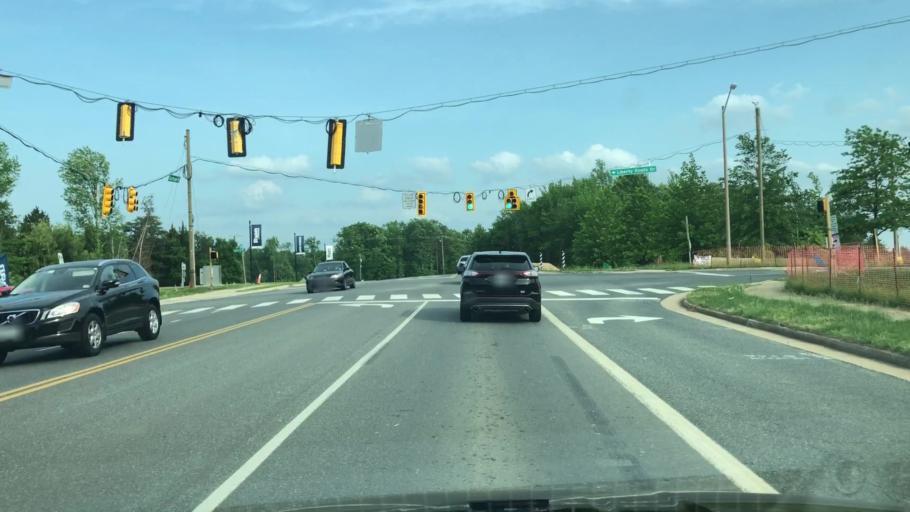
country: US
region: Virginia
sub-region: Stafford County
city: Stafford
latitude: 38.4354
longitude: -77.4498
